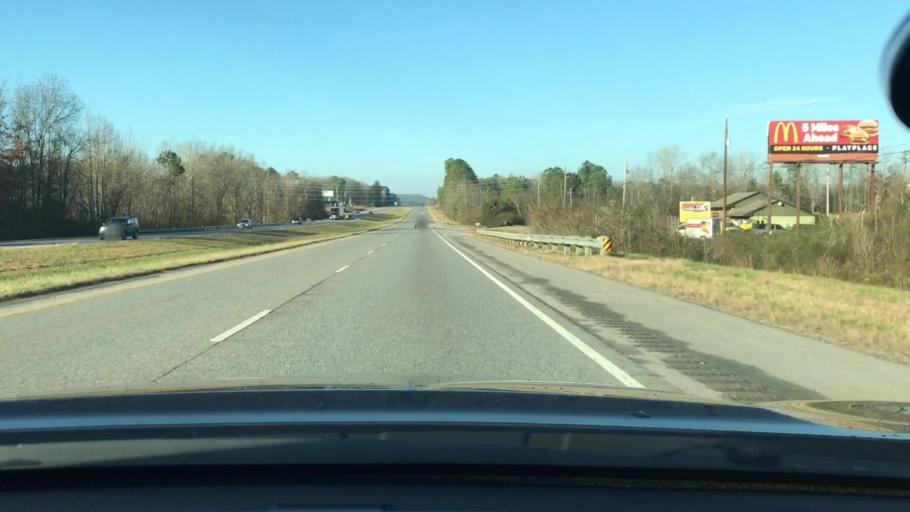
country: US
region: Alabama
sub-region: Shelby County
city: Westover
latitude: 33.3503
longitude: -86.5407
